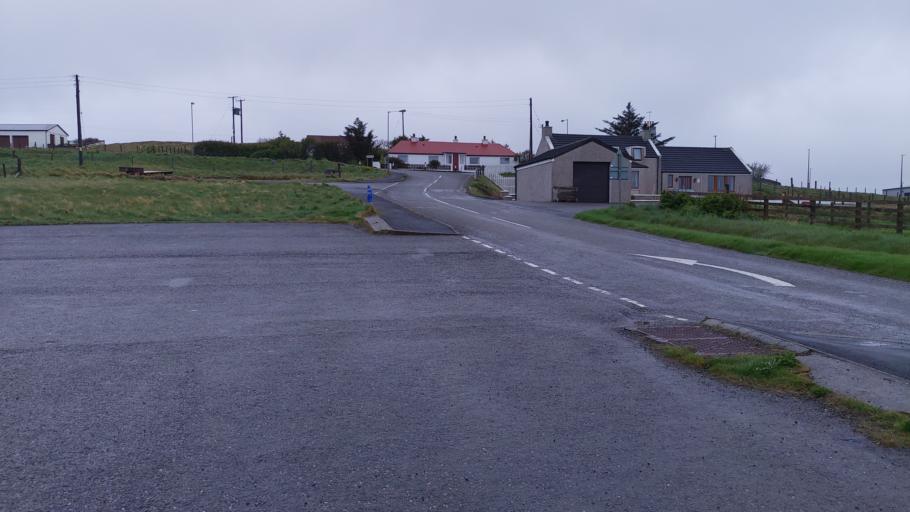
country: GB
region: Scotland
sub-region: Shetland Islands
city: Shetland
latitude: 60.5985
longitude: -1.0719
